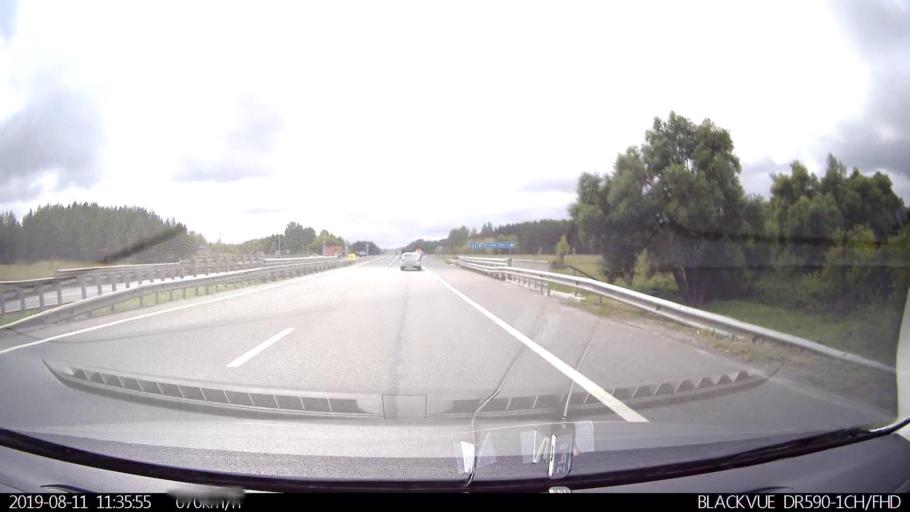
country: RU
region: Ulyanovsk
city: Silikatnyy
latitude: 54.0014
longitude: 48.2209
